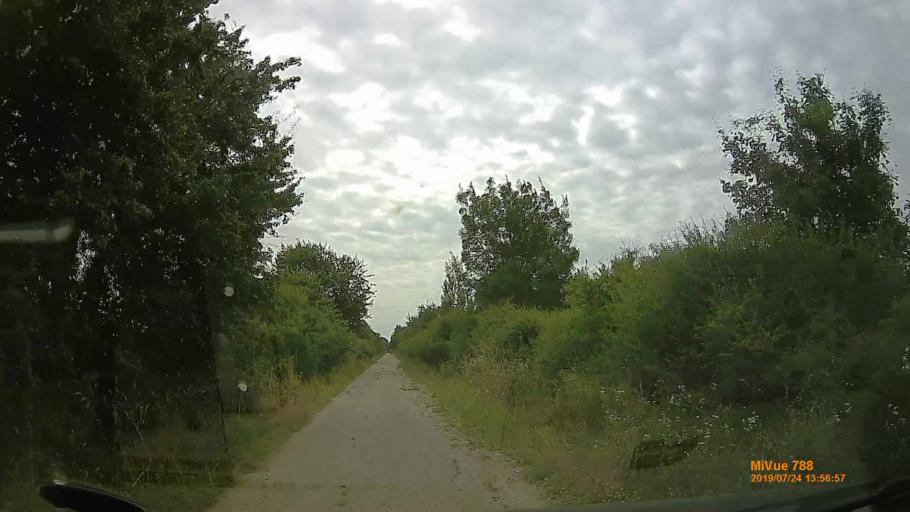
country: HU
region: Szabolcs-Szatmar-Bereg
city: Aranyosapati
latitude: 48.2634
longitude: 22.3312
